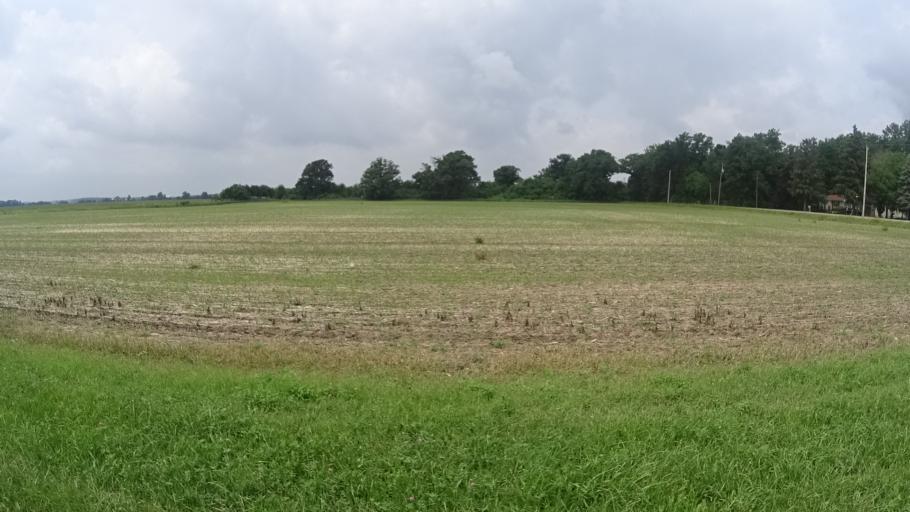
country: US
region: Ohio
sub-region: Huron County
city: Bellevue
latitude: 41.3253
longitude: -82.8054
